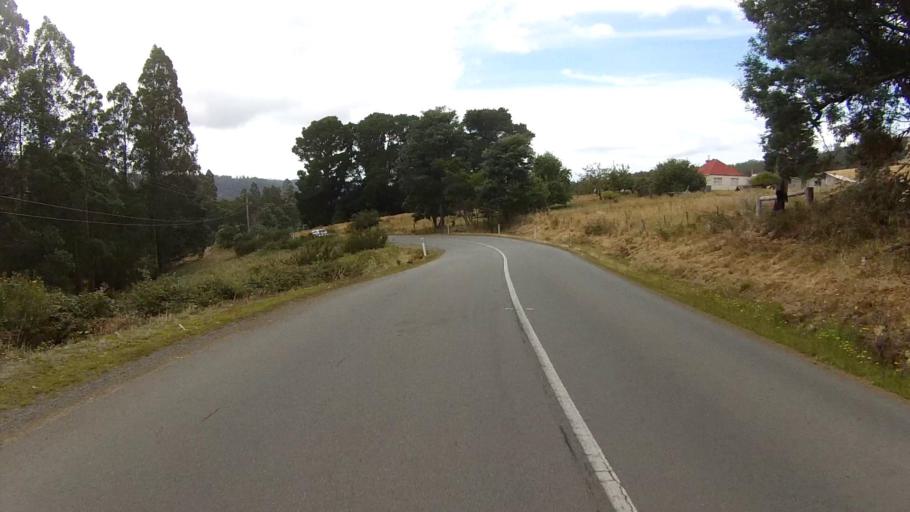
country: AU
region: Tasmania
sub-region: Kingborough
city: Kettering
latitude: -43.1132
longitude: 147.1936
